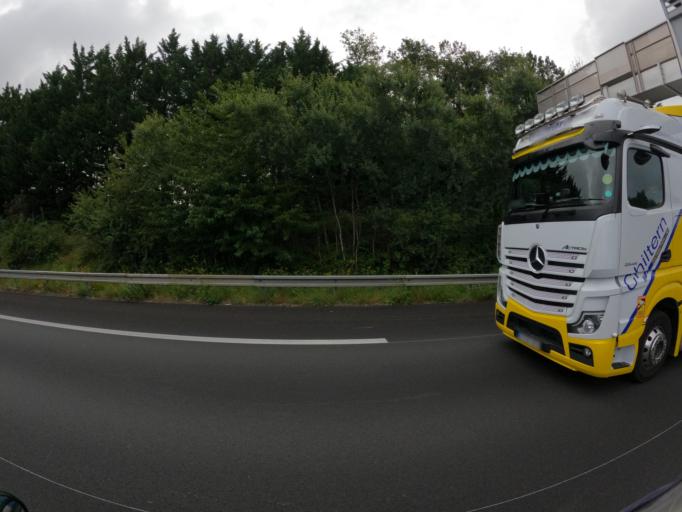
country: FR
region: Centre
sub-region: Departement d'Indre-et-Loire
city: Rochecorbon
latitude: 47.4174
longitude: 0.7306
